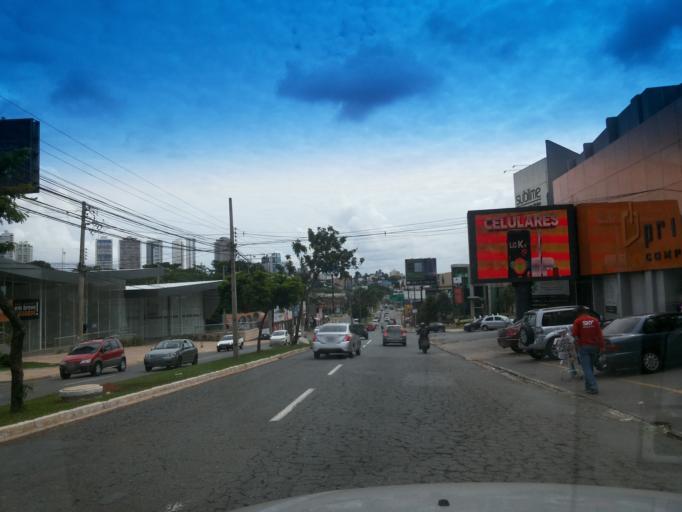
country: BR
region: Goias
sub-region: Goiania
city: Goiania
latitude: -16.7032
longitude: -49.2427
